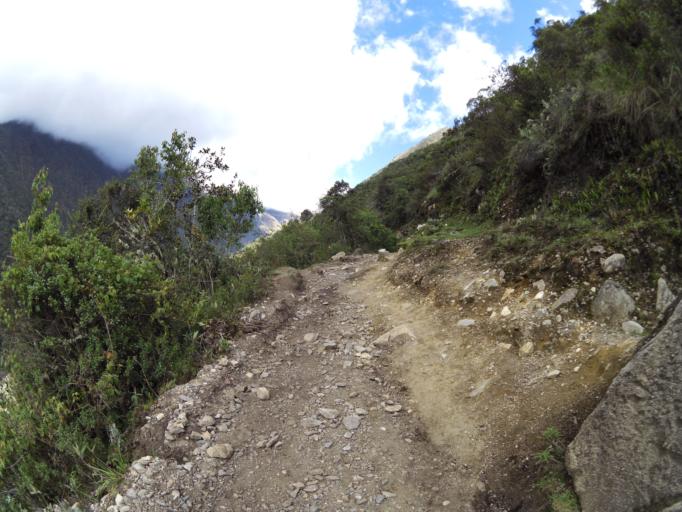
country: PE
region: Cusco
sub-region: Provincia de La Convencion
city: Santa Teresa
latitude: -13.3139
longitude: -72.6293
